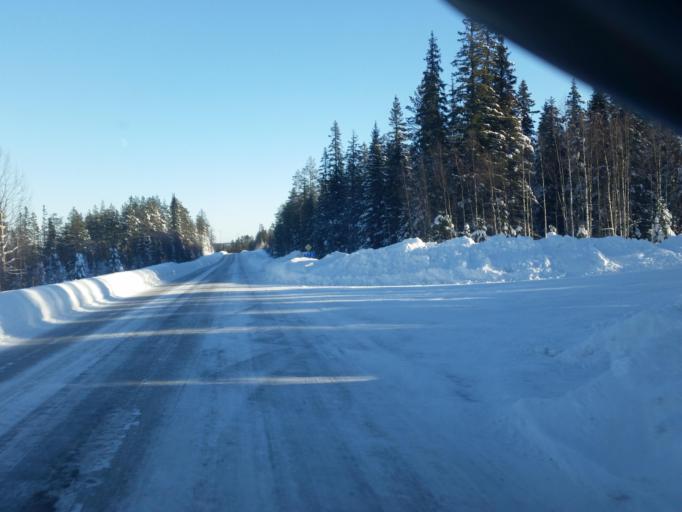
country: SE
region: Vaesterbotten
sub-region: Skelleftea Kommun
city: Storvik
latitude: 65.3304
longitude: 20.8325
